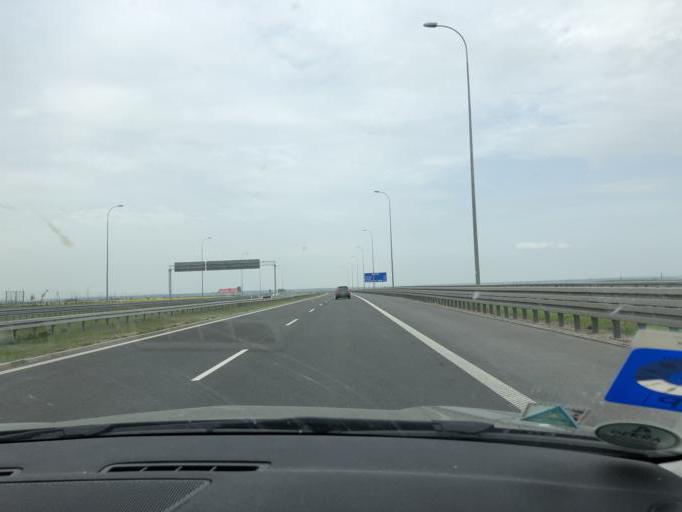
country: PL
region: Subcarpathian Voivodeship
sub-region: Powiat przeworski
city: Mirocin
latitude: 50.0504
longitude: 22.5710
